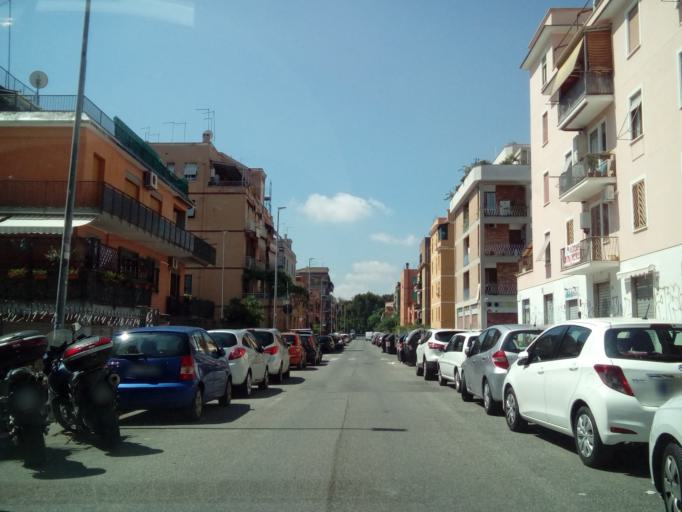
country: IT
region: Latium
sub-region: Citta metropolitana di Roma Capitale
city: Rome
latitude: 41.8768
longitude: 12.5707
